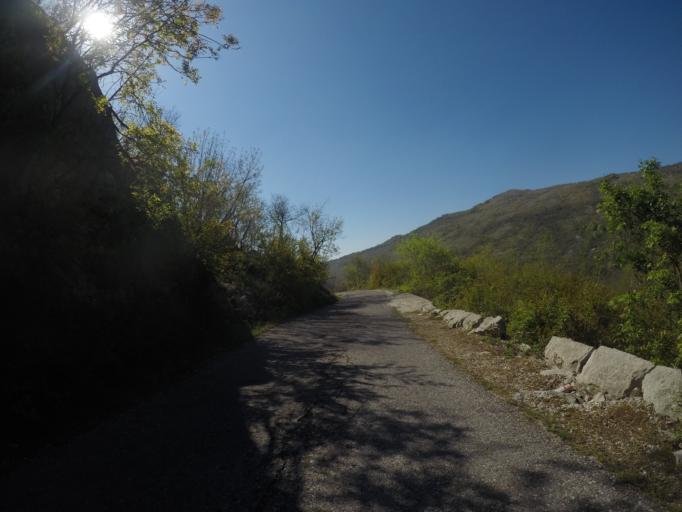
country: ME
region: Danilovgrad
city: Danilovgrad
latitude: 42.5158
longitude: 19.0689
